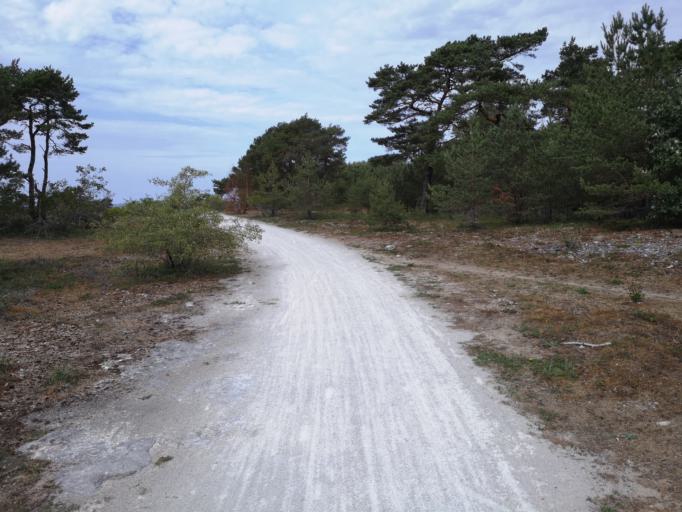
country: SE
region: Gotland
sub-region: Gotland
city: Vibble
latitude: 57.6147
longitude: 18.2599
